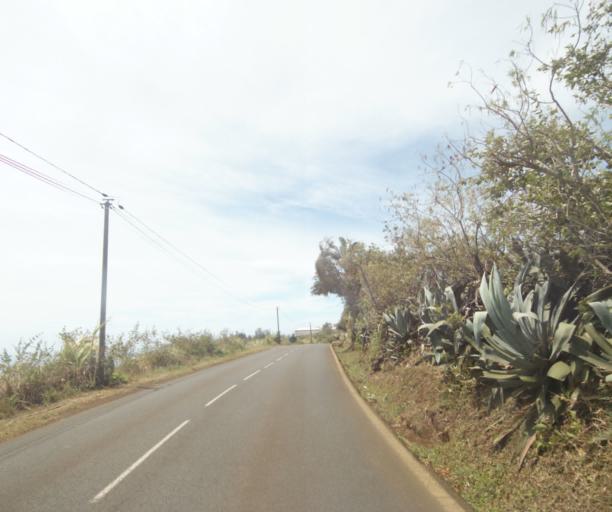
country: RE
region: Reunion
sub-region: Reunion
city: Saint-Paul
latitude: -21.0423
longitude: 55.2876
